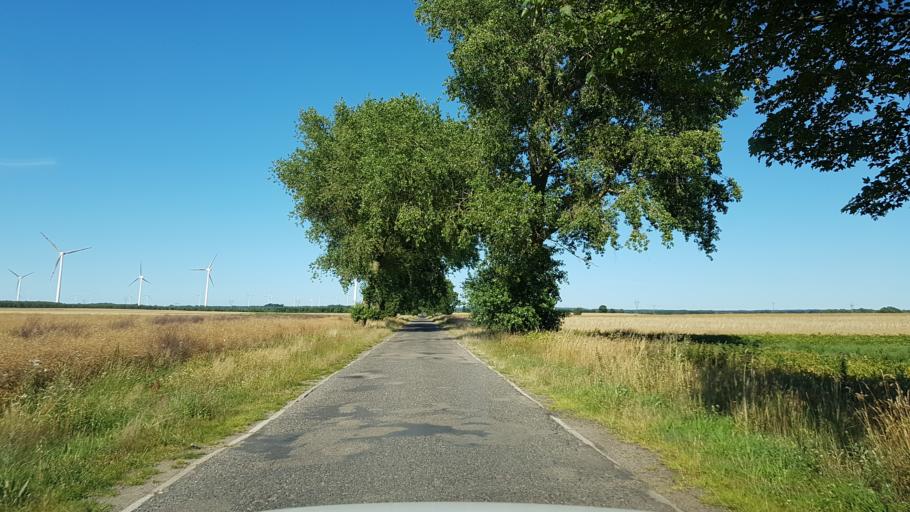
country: PL
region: West Pomeranian Voivodeship
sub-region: Powiat kamienski
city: Wolin
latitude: 53.7862
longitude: 14.6336
